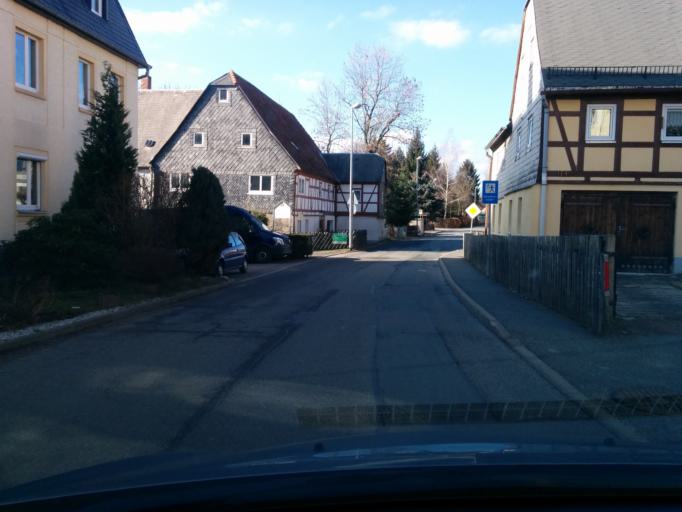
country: DE
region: Saxony
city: Neukirchen
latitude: 50.7838
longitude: 12.8528
